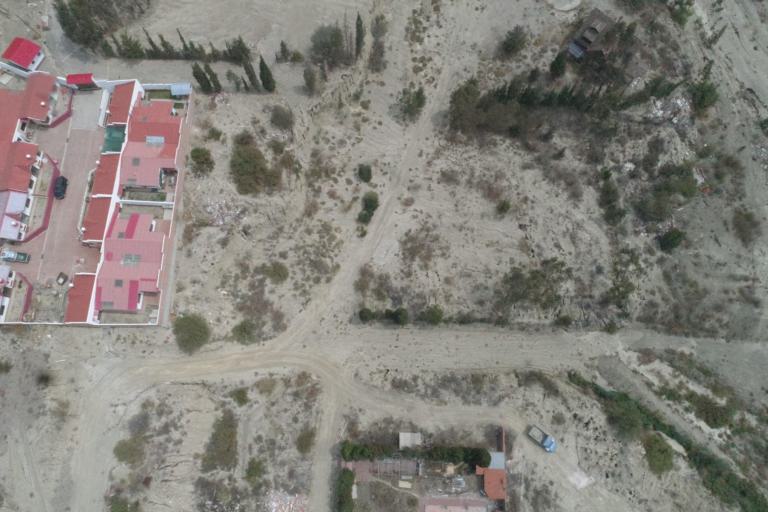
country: BO
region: La Paz
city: La Paz
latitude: -16.5984
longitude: -68.0683
